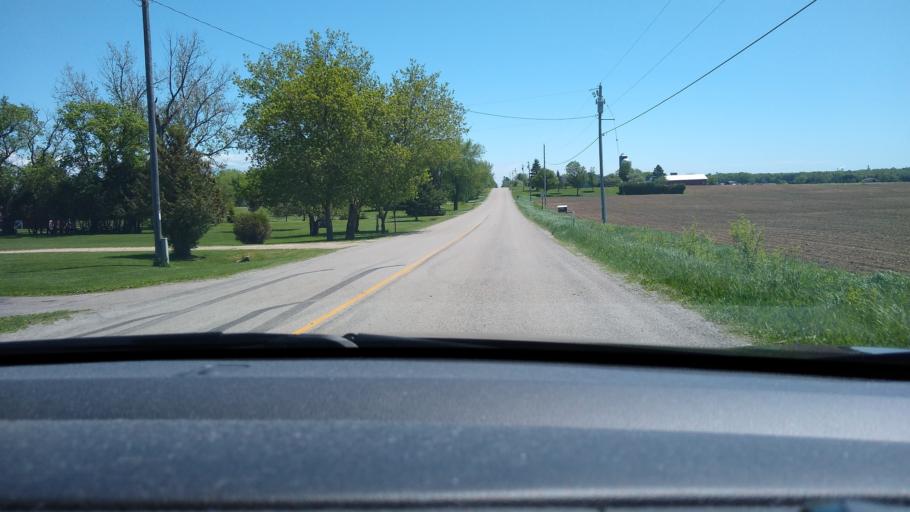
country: US
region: Michigan
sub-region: Delta County
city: Escanaba
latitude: 45.8261
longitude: -87.1569
